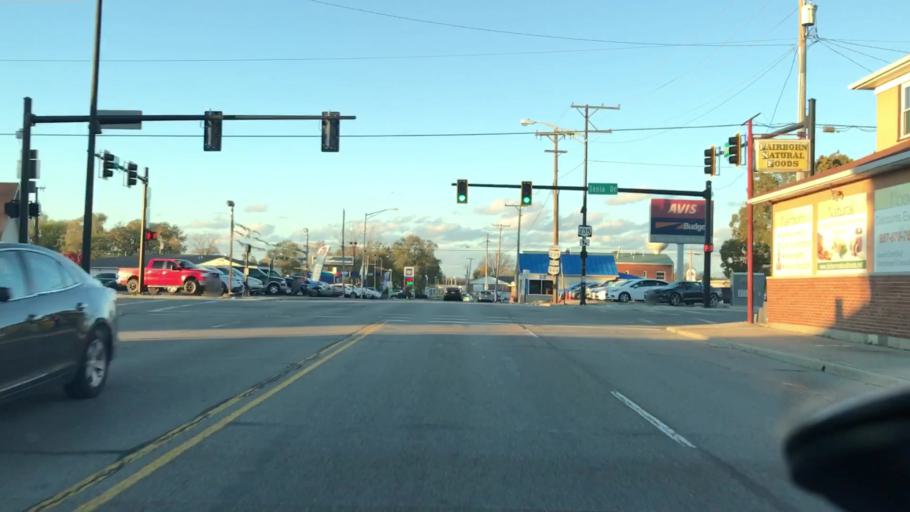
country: US
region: Ohio
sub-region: Greene County
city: Fairborn
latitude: 39.8250
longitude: -84.0274
